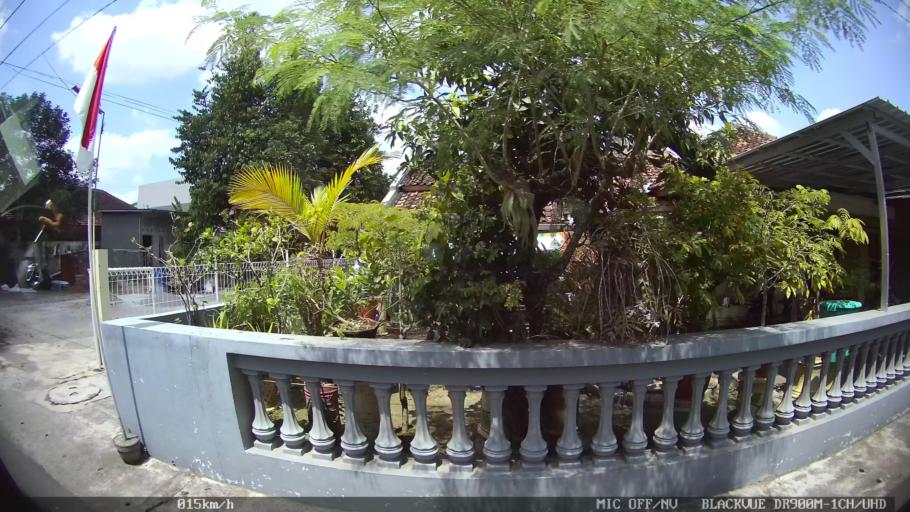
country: ID
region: Daerah Istimewa Yogyakarta
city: Gamping Lor
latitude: -7.8042
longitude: 110.3471
